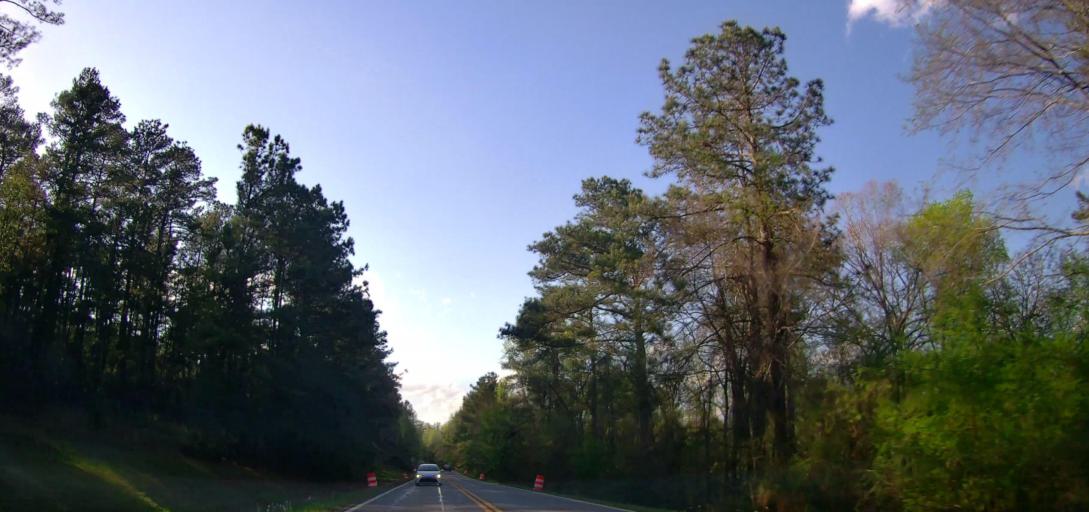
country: US
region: Georgia
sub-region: Baldwin County
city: Milledgeville
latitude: 33.1196
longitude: -83.2904
